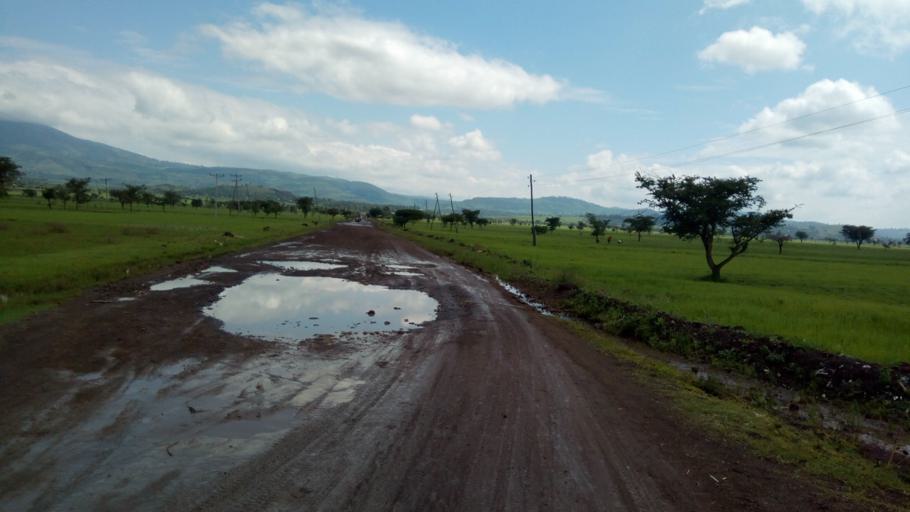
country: ET
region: Oromiya
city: Bishoftu
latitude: 8.8052
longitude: 39.0035
